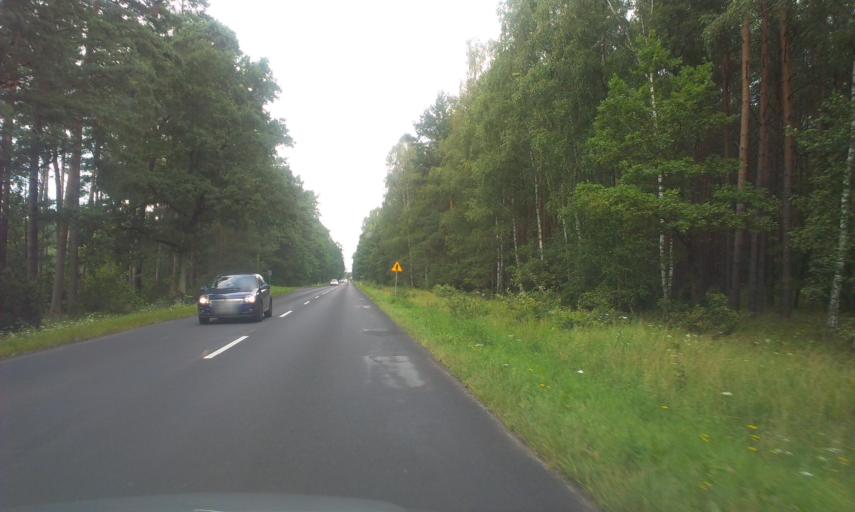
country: PL
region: West Pomeranian Voivodeship
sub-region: Powiat bialogardzki
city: Bialogard
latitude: 53.9680
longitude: 16.0464
